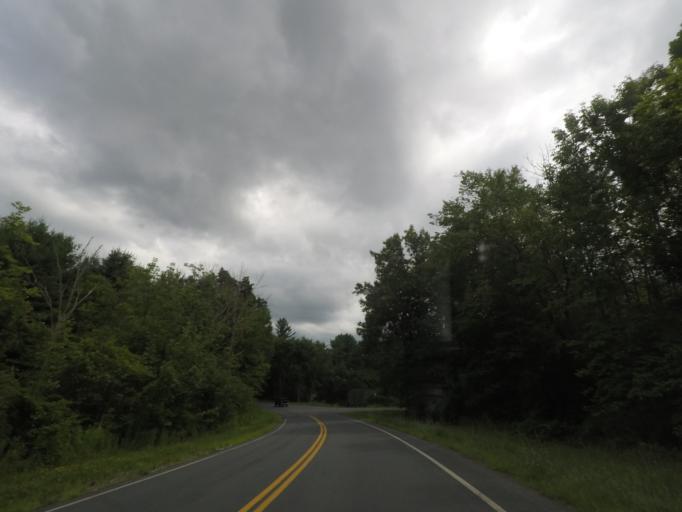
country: US
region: New York
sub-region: Saratoga County
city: Stillwater
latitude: 42.8701
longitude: -73.5599
